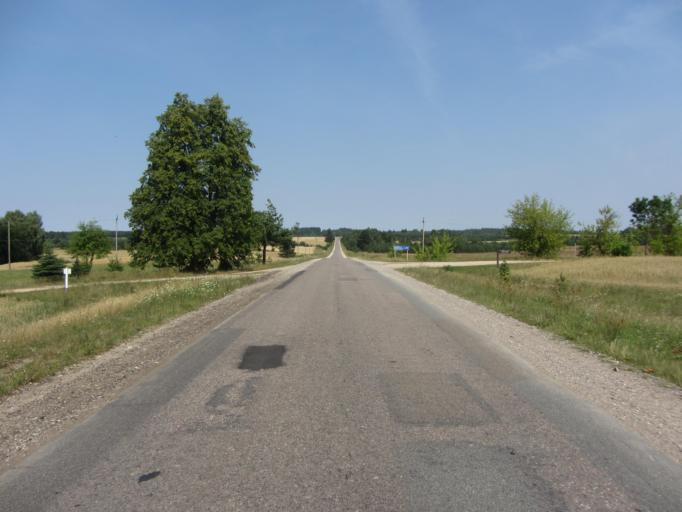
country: LT
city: Veisiejai
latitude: 54.0623
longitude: 23.6532
